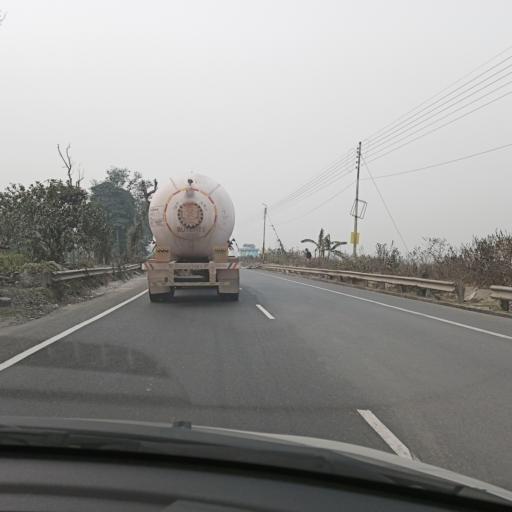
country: IN
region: West Bengal
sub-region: Darjiling
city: Shiliguri
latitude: 26.6521
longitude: 88.4068
